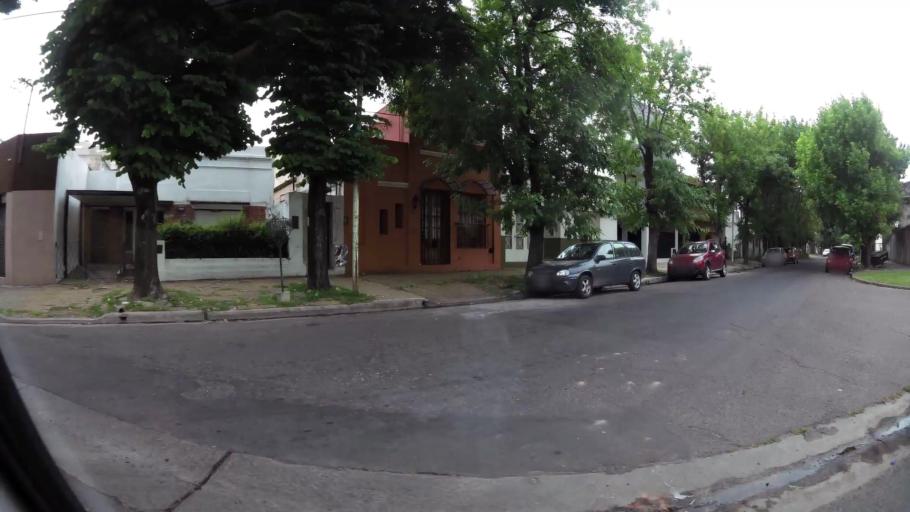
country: AR
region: Buenos Aires
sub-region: Partido de La Plata
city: La Plata
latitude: -34.9333
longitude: -57.9625
